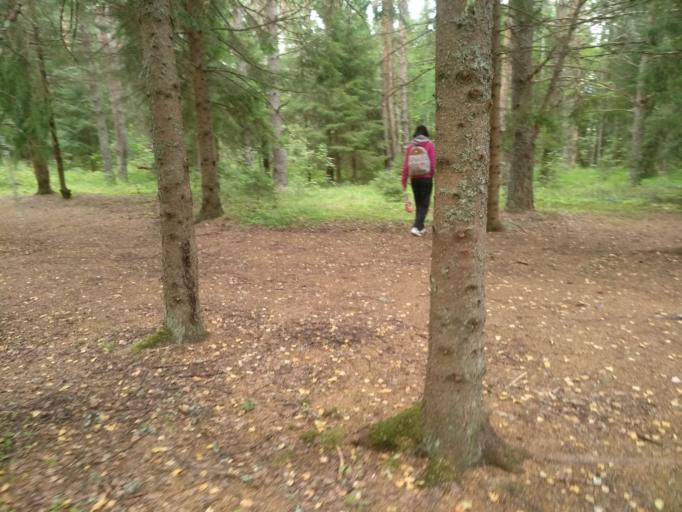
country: EE
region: Harju
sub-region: Anija vald
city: Kehra
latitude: 59.1886
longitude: 25.5119
